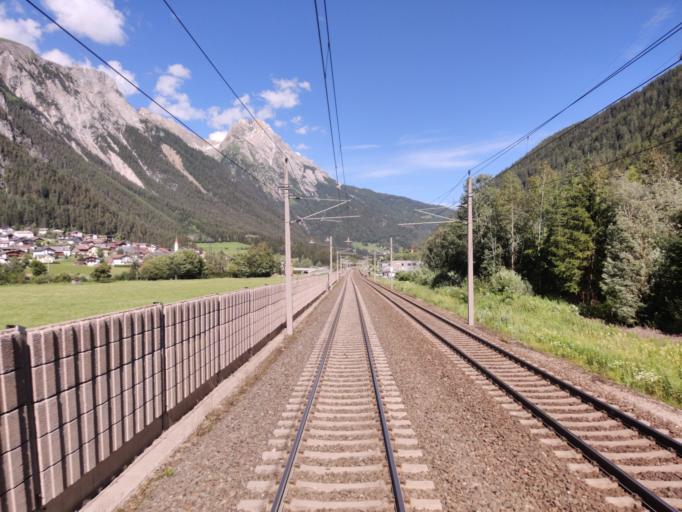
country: AT
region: Tyrol
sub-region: Politischer Bezirk Landeck
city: Flirsch
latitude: 47.1497
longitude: 10.3713
